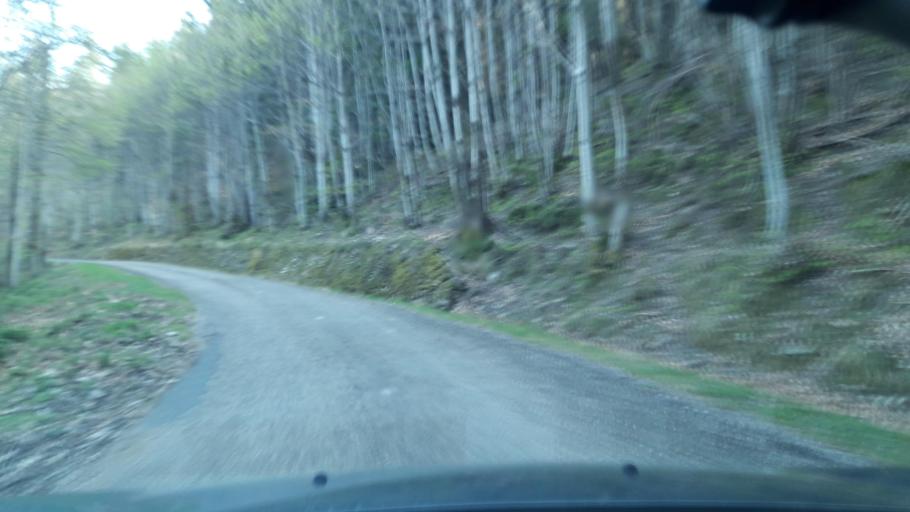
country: FR
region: Languedoc-Roussillon
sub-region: Departement du Gard
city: Valleraugue
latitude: 44.1039
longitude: 3.6627
